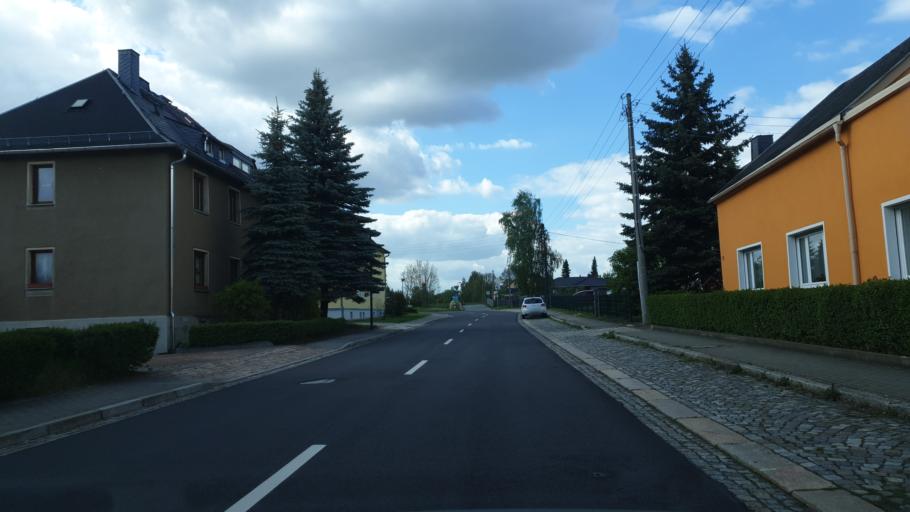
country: DE
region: Saxony
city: Lugau
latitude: 50.7253
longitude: 12.7422
